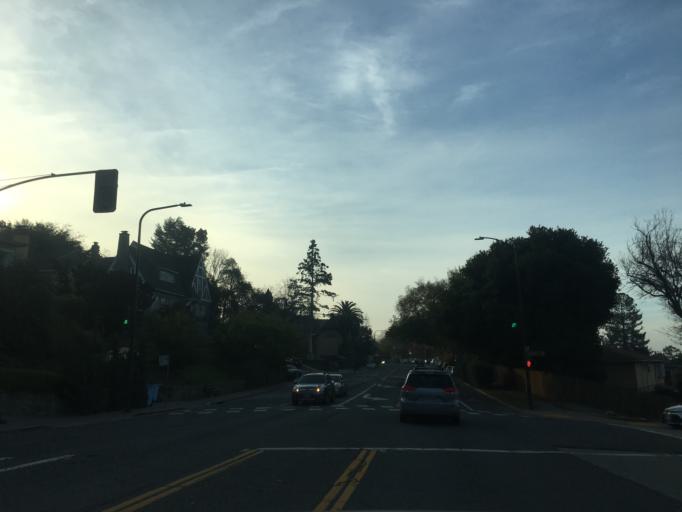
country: US
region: California
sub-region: Alameda County
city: Berkeley
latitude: 37.8887
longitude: -122.2724
